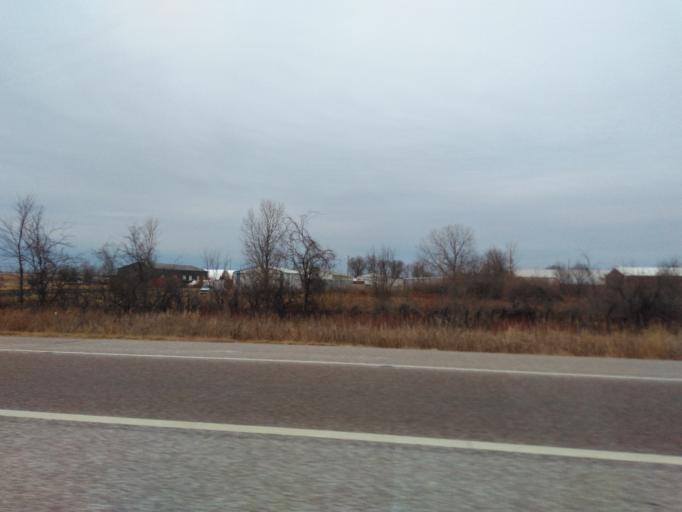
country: US
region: Illinois
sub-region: Saint Clair County
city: Washington Park
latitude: 38.6190
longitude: -90.0621
